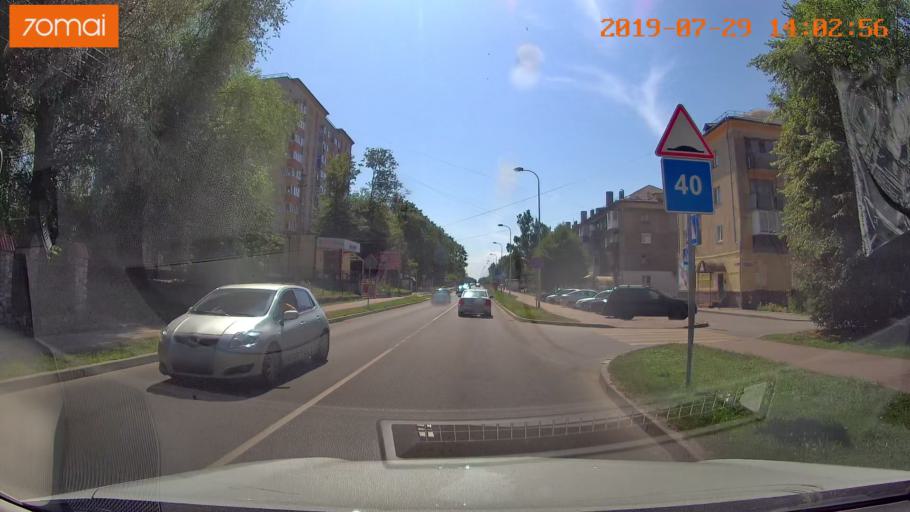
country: RU
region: Kaliningrad
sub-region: Gorod Kaliningrad
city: Baltiysk
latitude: 54.6606
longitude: 19.9148
